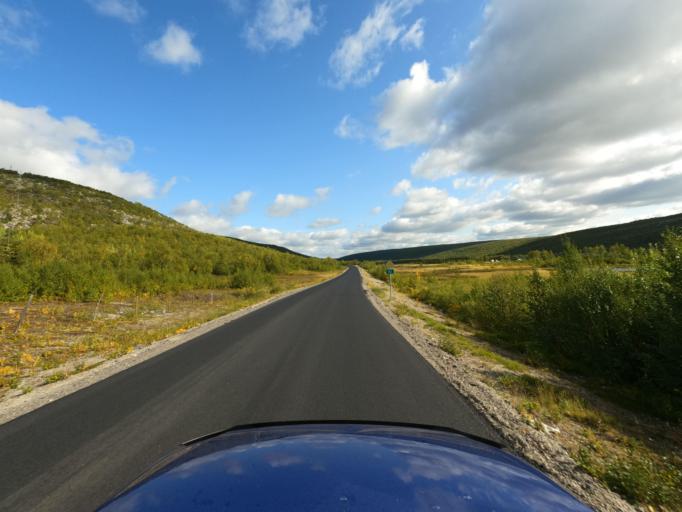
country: NO
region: Finnmark Fylke
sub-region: Porsanger
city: Lakselv
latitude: 69.4025
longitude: 24.6537
